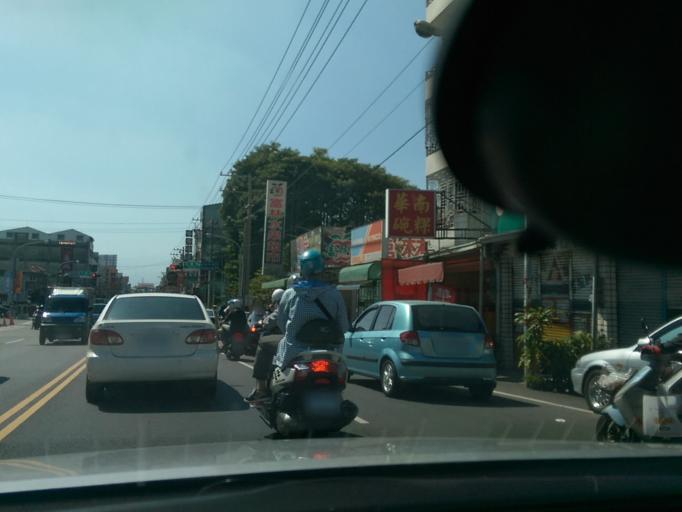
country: TW
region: Taiwan
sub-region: Chiayi
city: Jiayi Shi
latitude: 23.4643
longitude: 120.4552
